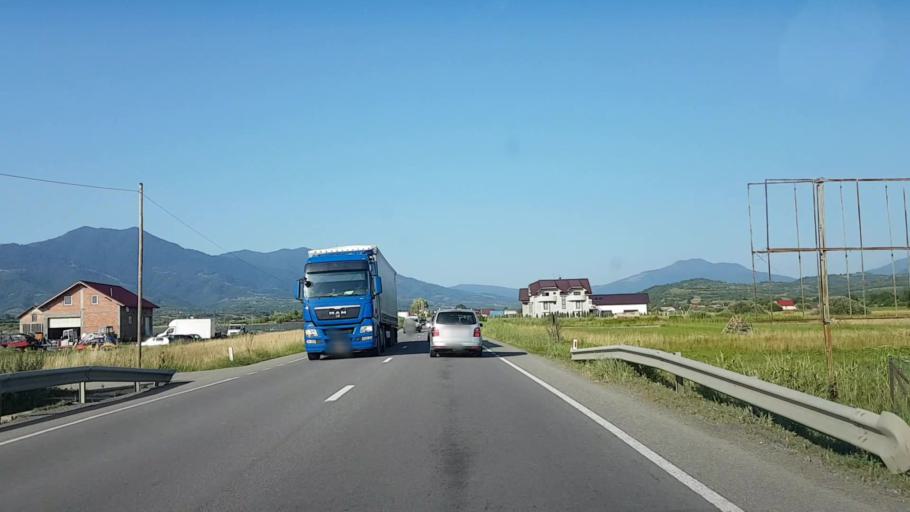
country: RO
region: Bistrita-Nasaud
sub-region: Comuna Josenii Bargaului
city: Josenii Bargaului
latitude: 47.2042
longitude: 24.6512
